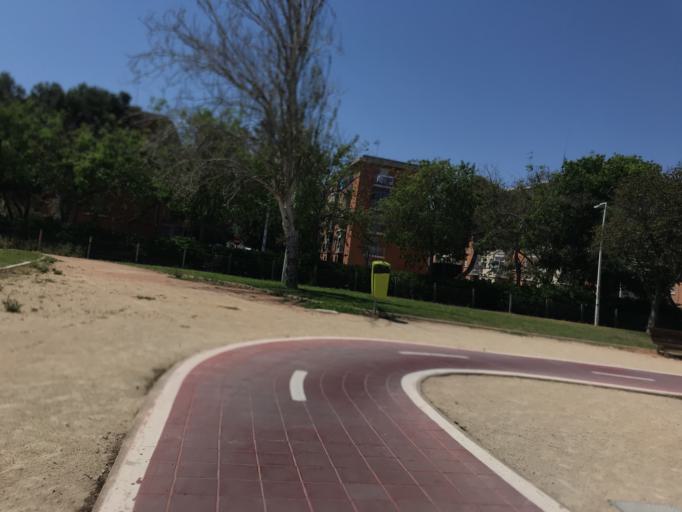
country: ES
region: Valencia
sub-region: Provincia de Valencia
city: Mislata
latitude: 39.4649
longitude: -0.4056
